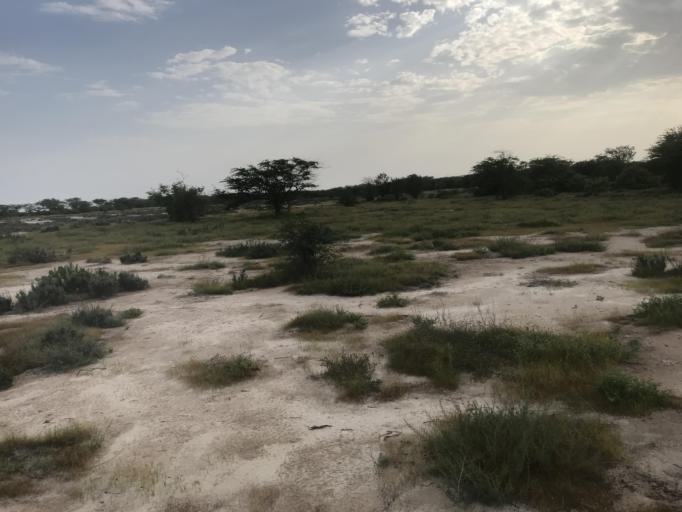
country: SN
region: Saint-Louis
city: Saint-Louis
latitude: 15.9315
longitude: -16.4641
